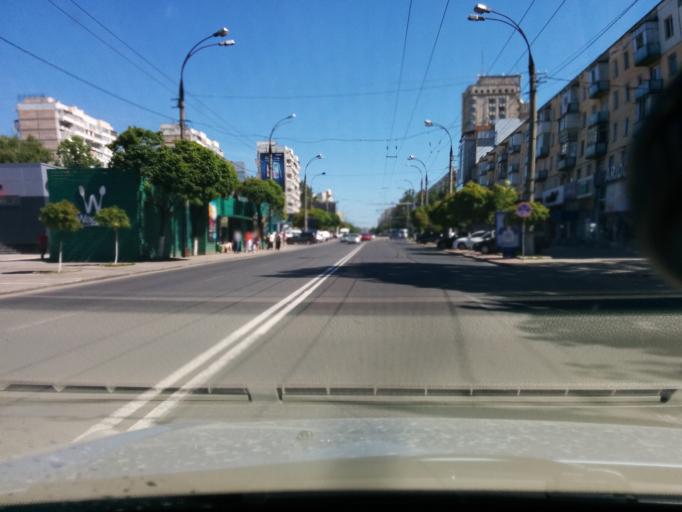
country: MD
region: Chisinau
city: Chisinau
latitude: 47.0426
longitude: 28.8607
